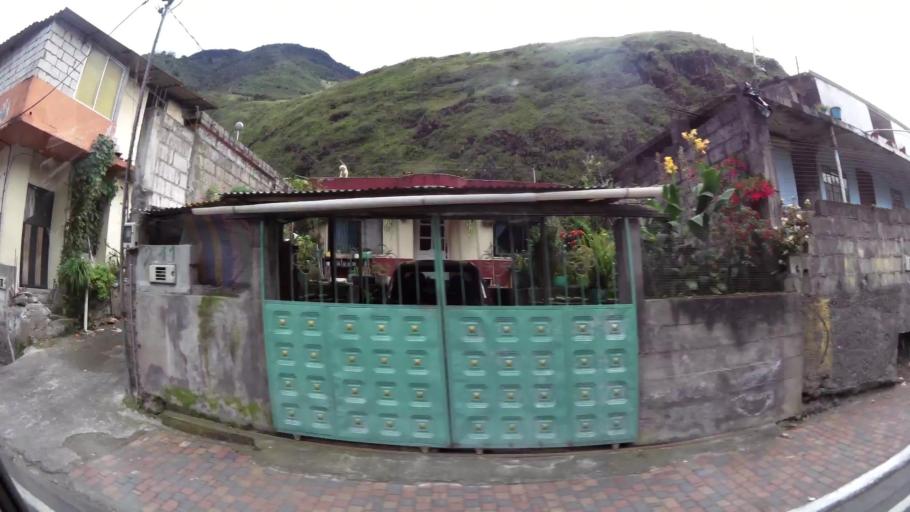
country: EC
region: Tungurahua
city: Banos
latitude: -1.3958
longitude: -78.3877
